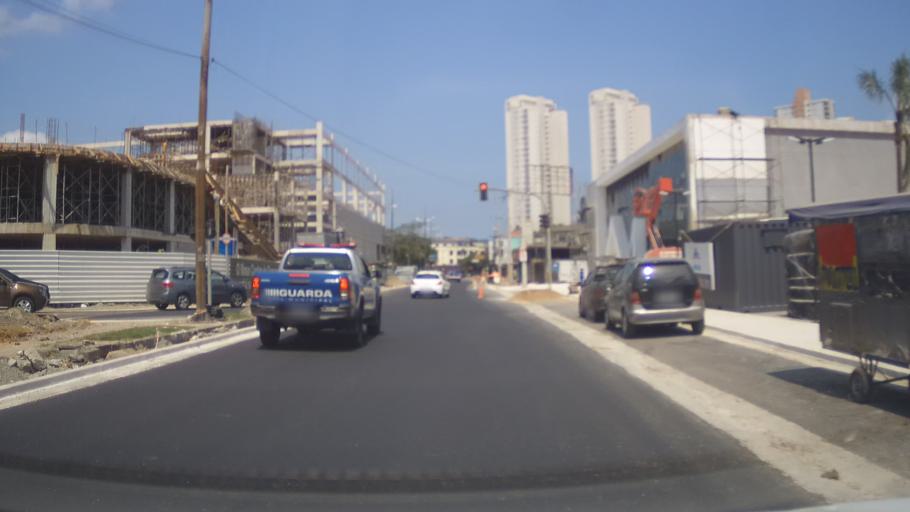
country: BR
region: Sao Paulo
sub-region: Guaruja
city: Guaruja
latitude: -23.9840
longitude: -46.2948
